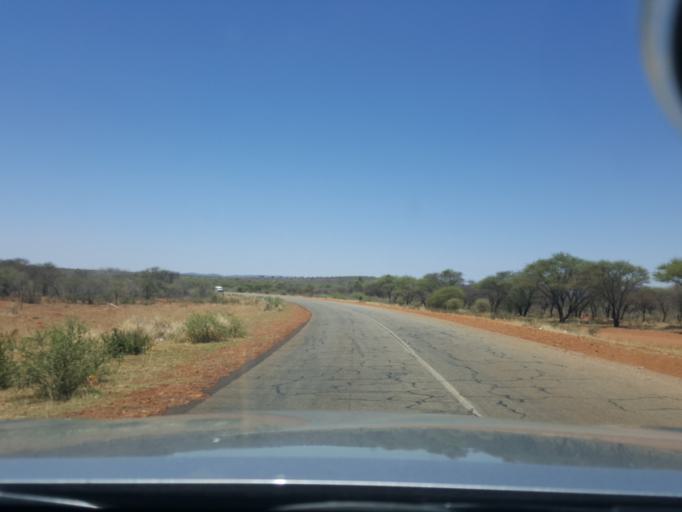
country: BW
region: South East
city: Otse
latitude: -25.1195
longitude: 25.9444
